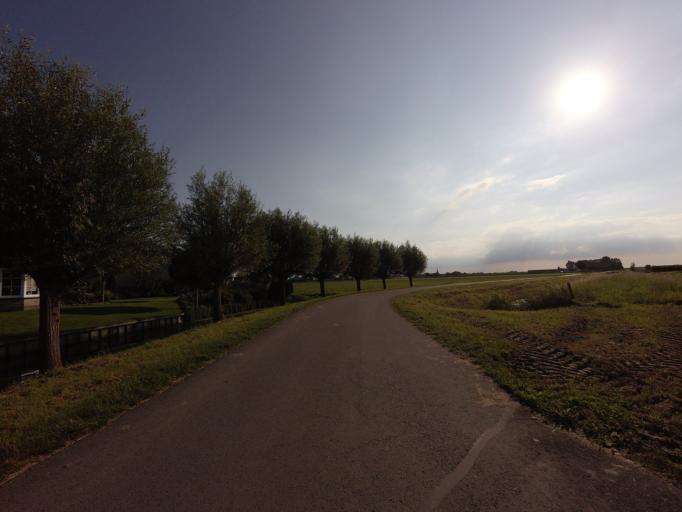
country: NL
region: North Holland
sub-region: Gemeente Hoorn
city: Hoorn
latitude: 52.6793
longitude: 5.1335
